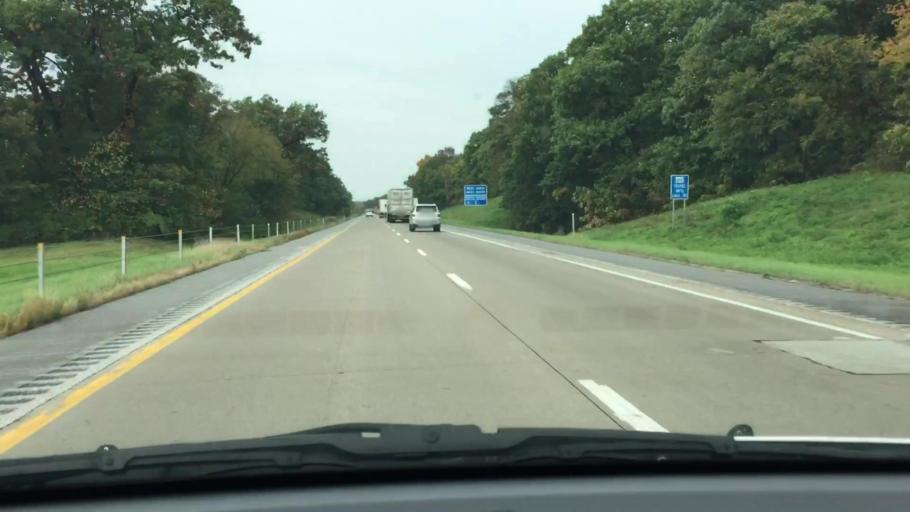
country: US
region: Iowa
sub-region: Muscatine County
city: Wilton
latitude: 41.6385
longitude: -91.0447
